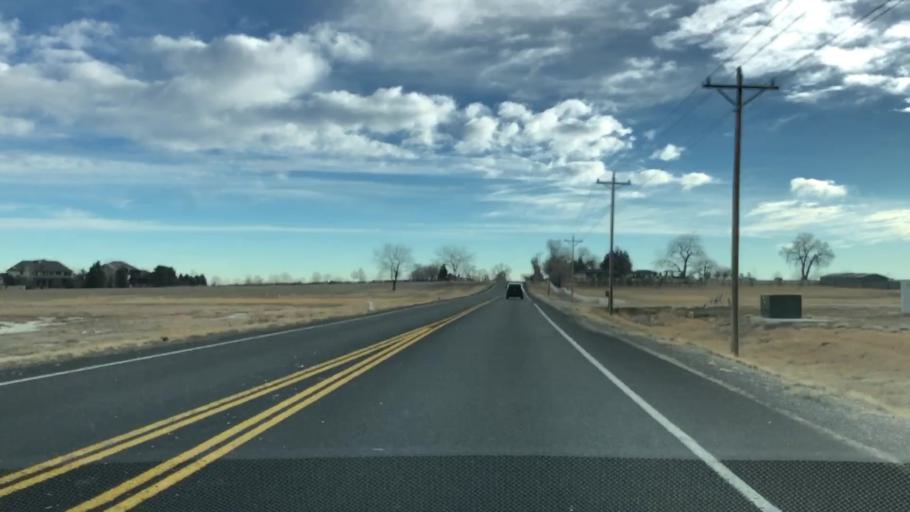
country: US
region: Colorado
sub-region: Larimer County
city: Loveland
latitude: 40.4652
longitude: -105.0097
